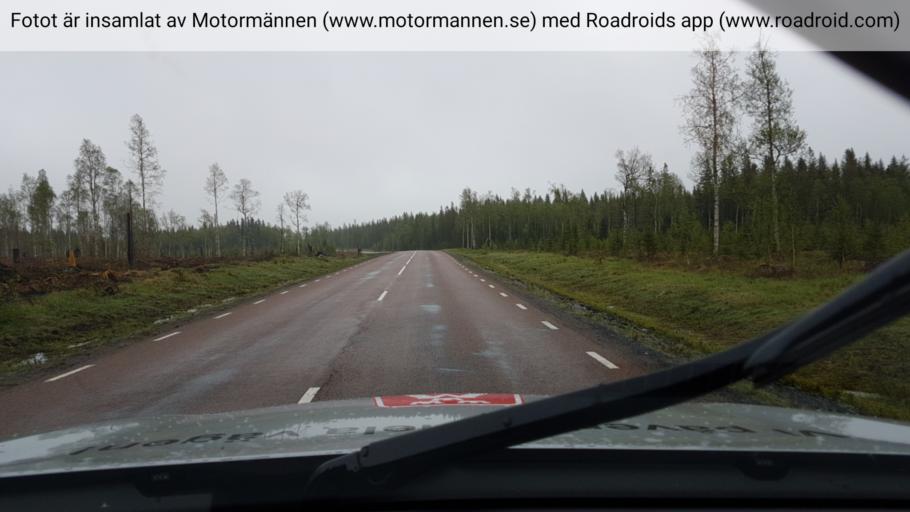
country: SE
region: Jaemtland
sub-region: Krokoms Kommun
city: Valla
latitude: 63.1361
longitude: 13.9366
